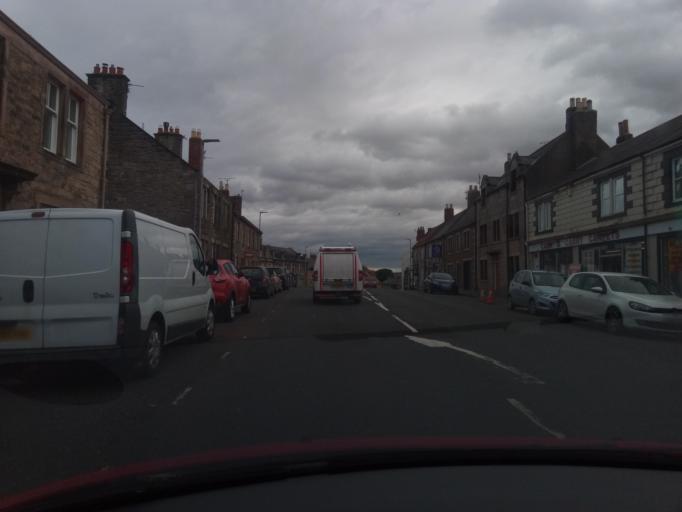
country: GB
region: England
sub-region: Northumberland
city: Berwick-Upon-Tweed
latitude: 55.7740
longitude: -2.0091
